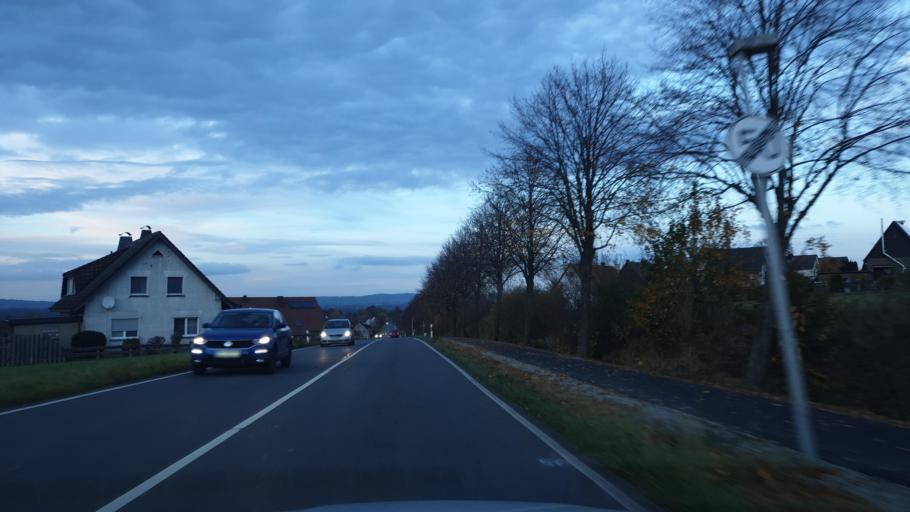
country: DE
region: North Rhine-Westphalia
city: Spenge
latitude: 52.1629
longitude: 8.5026
